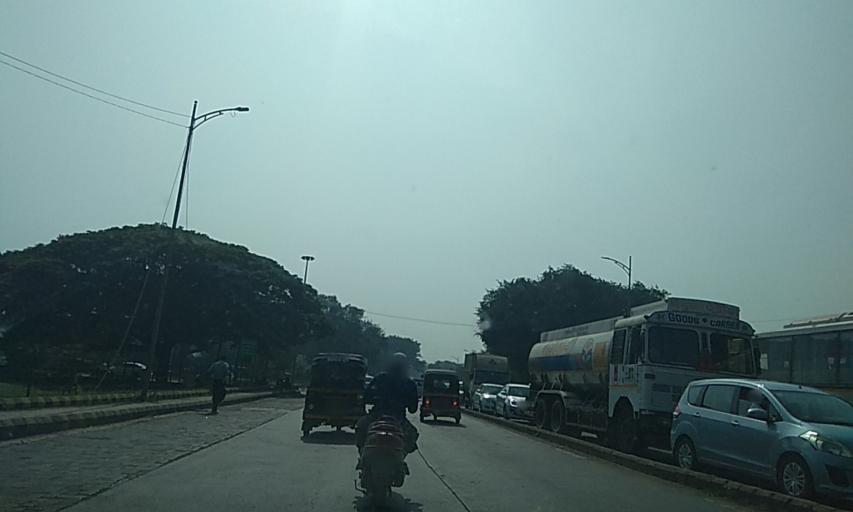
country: IN
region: Maharashtra
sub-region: Pune Division
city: Khadki
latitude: 18.5569
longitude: 73.8467
